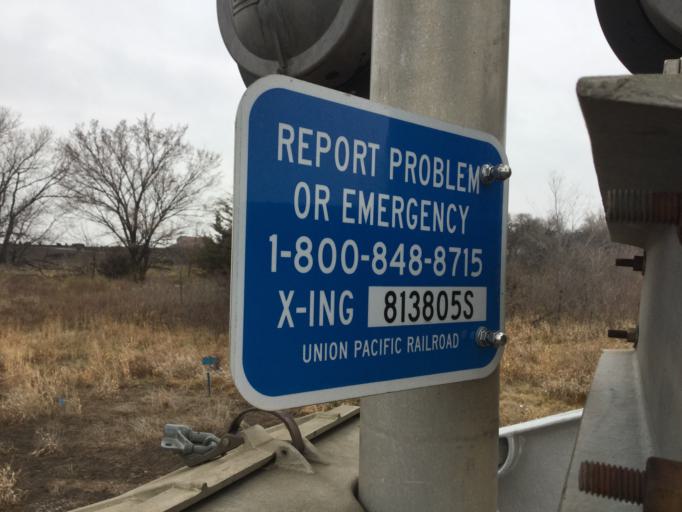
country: US
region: Kansas
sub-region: Marshall County
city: Marysville
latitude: 39.9042
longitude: -96.8434
